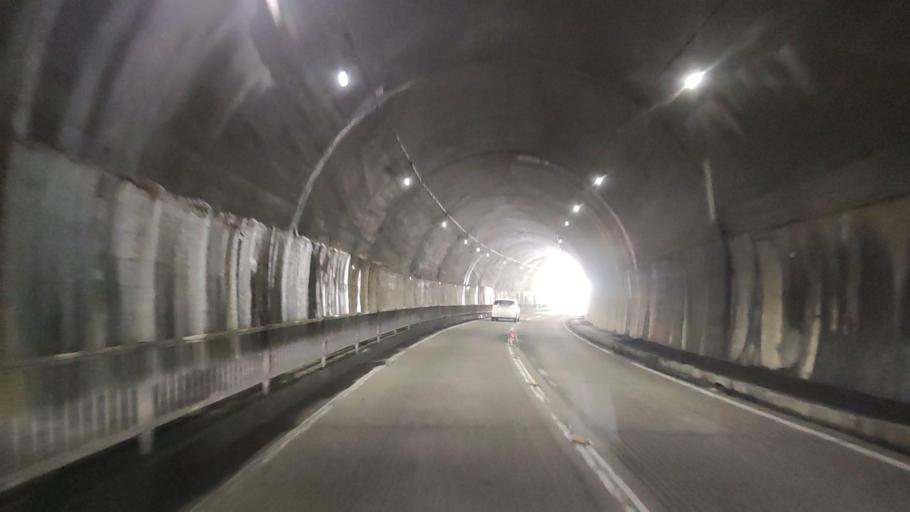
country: JP
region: Mie
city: Owase
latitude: 34.1793
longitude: 136.0045
